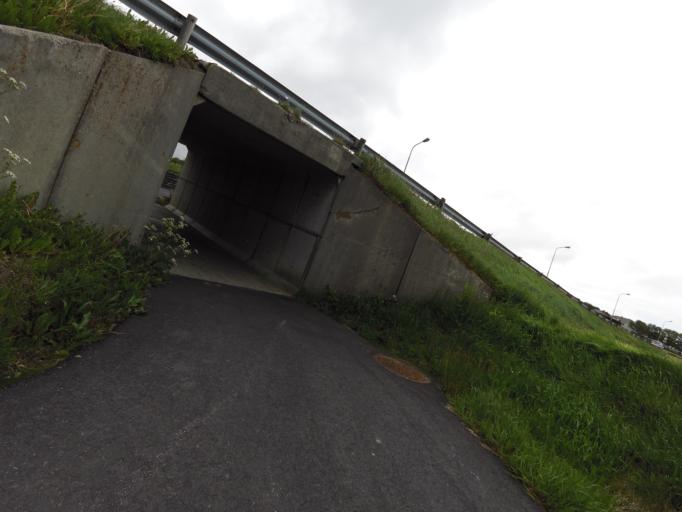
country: NO
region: Rogaland
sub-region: Klepp
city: Kleppe
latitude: 58.8322
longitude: 5.5971
